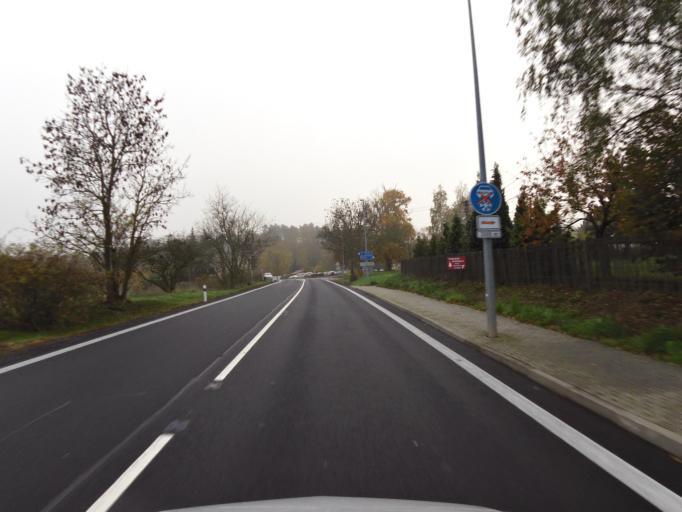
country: CZ
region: Ustecky
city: Chlumec
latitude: 50.7123
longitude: 13.9583
